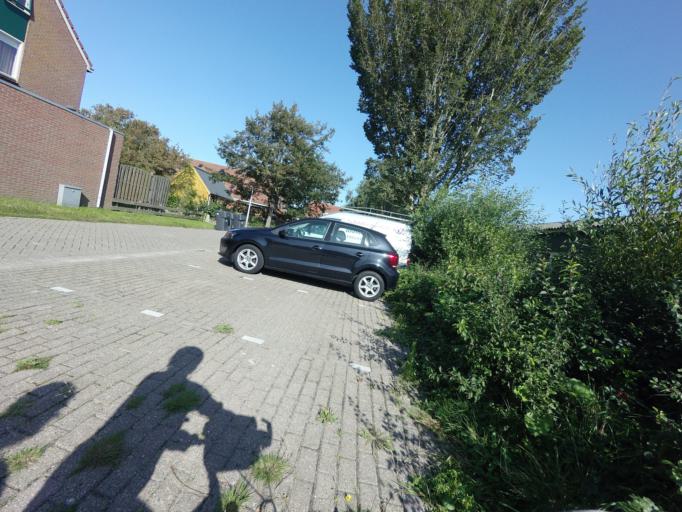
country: NL
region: Friesland
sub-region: Gemeente Terschelling
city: West-Terschelling
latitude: 53.3819
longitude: 5.2887
